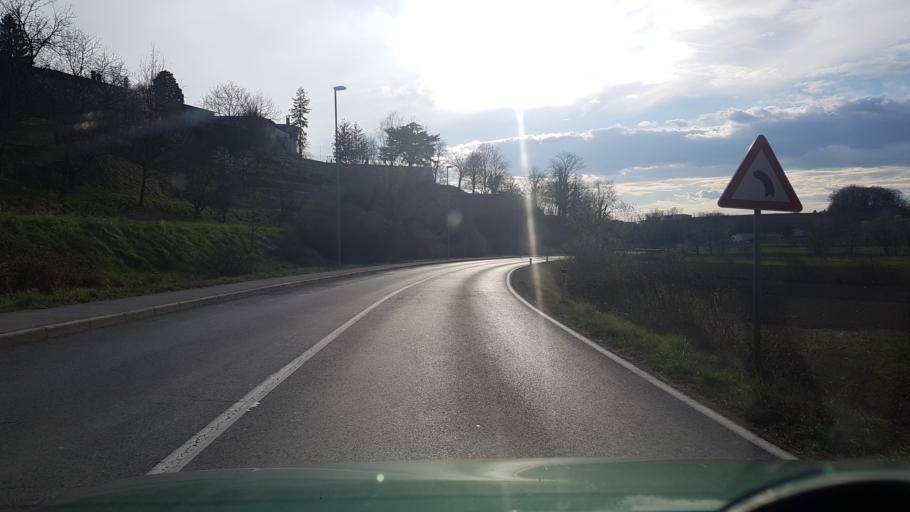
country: SI
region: Nova Gorica
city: Prvacina
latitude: 45.9075
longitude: 13.7023
